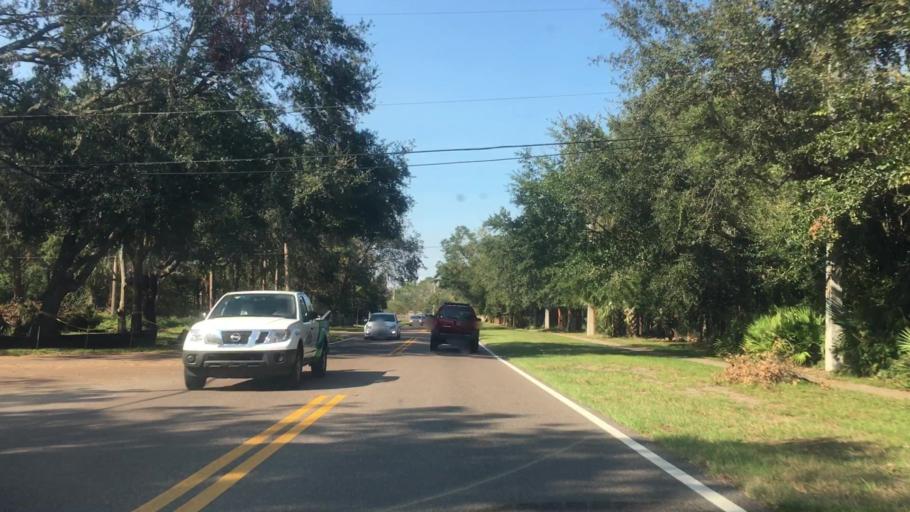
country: US
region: Florida
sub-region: Duval County
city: Neptune Beach
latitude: 30.2954
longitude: -81.4378
